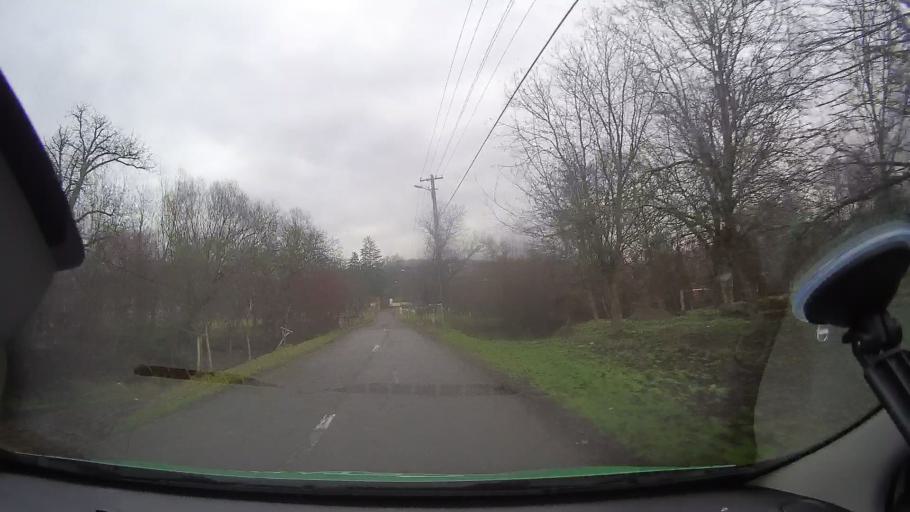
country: RO
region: Arad
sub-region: Comuna Brazii
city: Brazii
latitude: 46.2416
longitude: 22.3325
